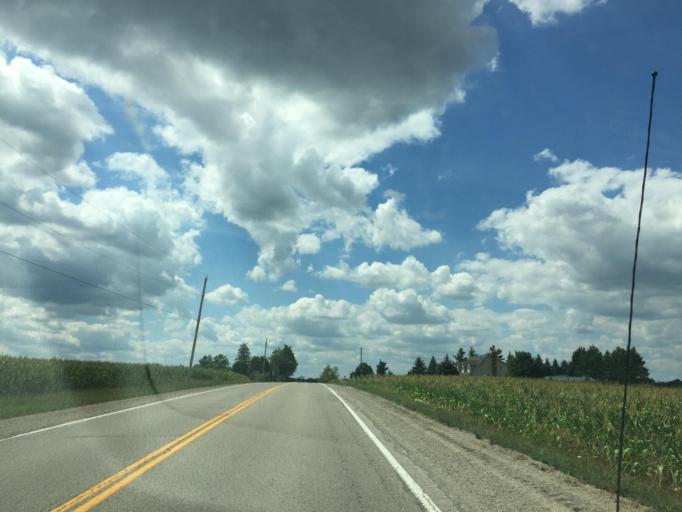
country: CA
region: Ontario
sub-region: Wellington County
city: Guelph
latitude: 43.5323
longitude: -80.3791
